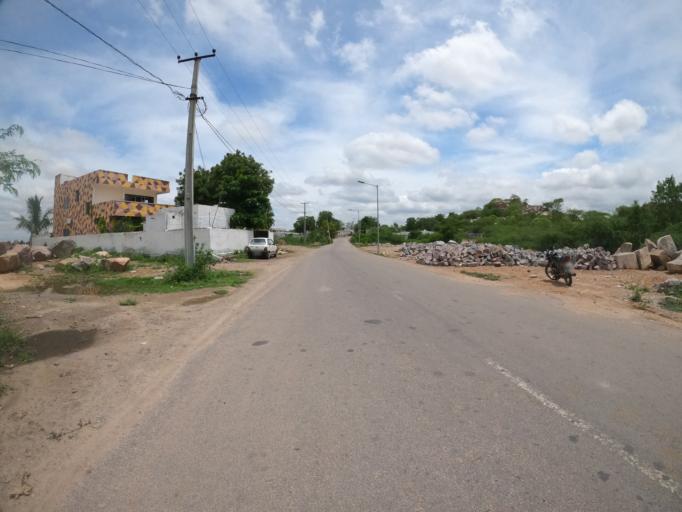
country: IN
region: Telangana
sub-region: Hyderabad
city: Hyderabad
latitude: 17.2971
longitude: 78.3791
